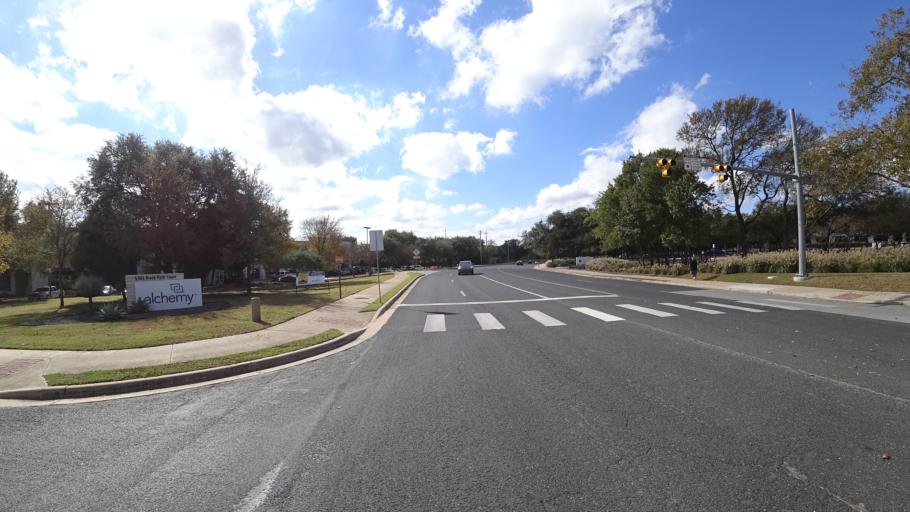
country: US
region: Texas
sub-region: Williamson County
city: Jollyville
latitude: 30.4325
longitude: -97.7331
